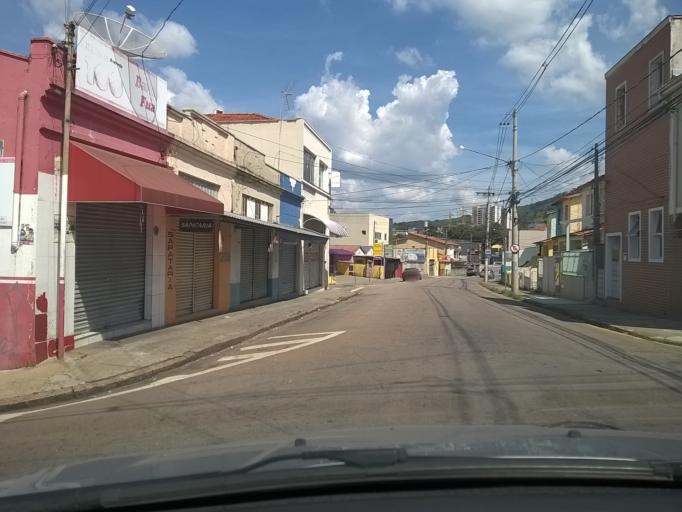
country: BR
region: Sao Paulo
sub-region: Jundiai
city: Jundiai
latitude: -23.2058
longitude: -46.8859
